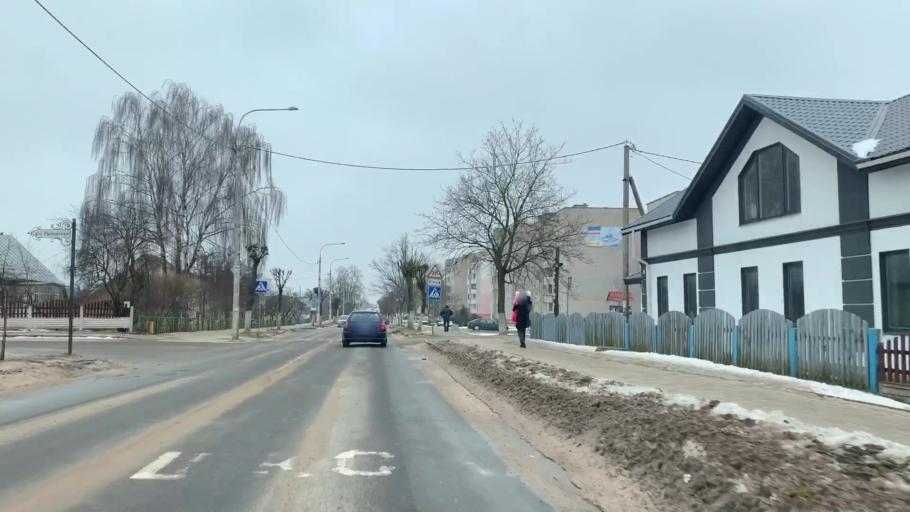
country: BY
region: Minsk
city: Nyasvizh
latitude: 53.2261
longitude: 26.6683
